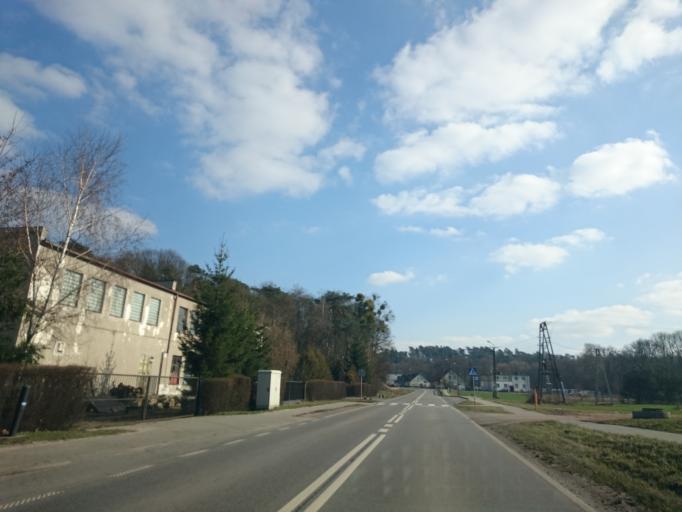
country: PL
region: Kujawsko-Pomorskie
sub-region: Grudziadz
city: Grudziadz
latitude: 53.4386
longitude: 18.8266
